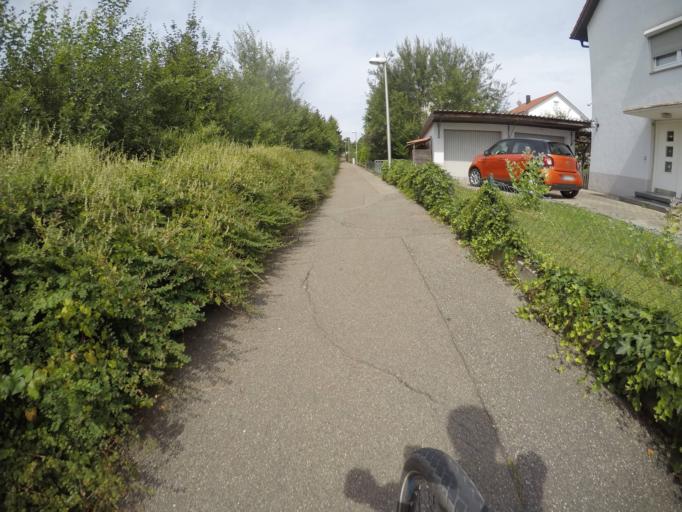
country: DE
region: Baden-Wuerttemberg
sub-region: Karlsruhe Region
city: Gondelsheim
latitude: 49.1033
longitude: 8.6480
